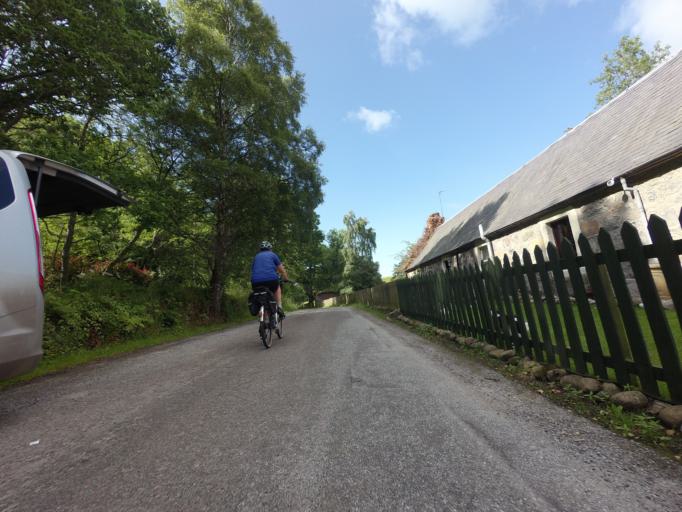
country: GB
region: Scotland
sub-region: Highland
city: Nairn
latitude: 57.5427
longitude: -3.8657
